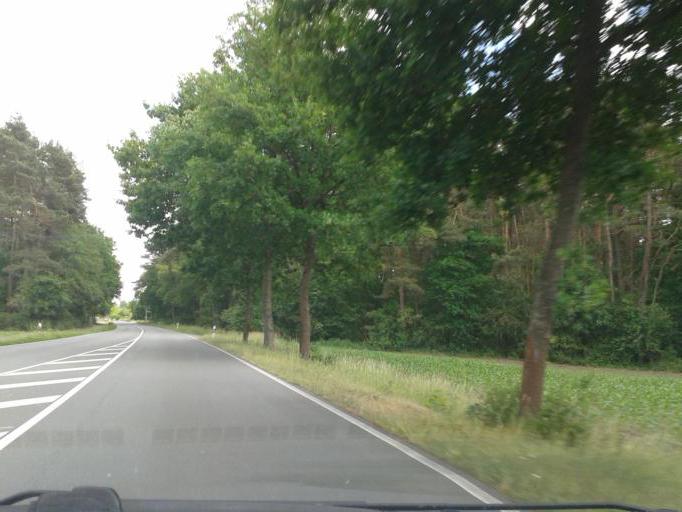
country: DE
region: North Rhine-Westphalia
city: Bad Lippspringe
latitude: 51.7744
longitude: 8.7880
